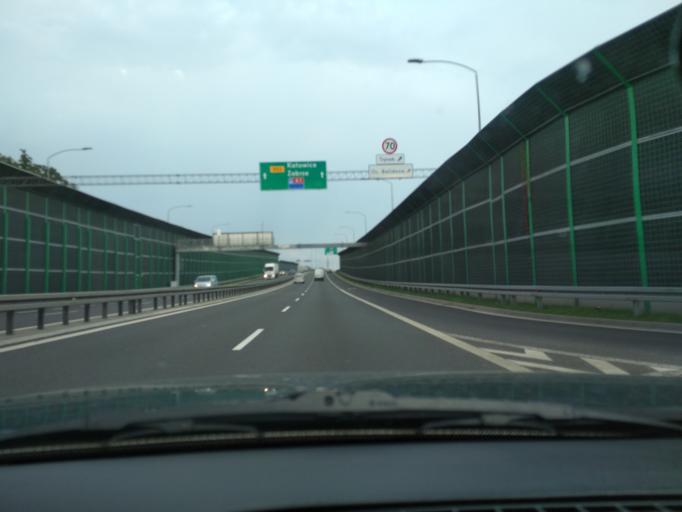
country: PL
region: Silesian Voivodeship
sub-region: Gliwice
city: Gliwice
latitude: 50.2906
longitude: 18.6963
